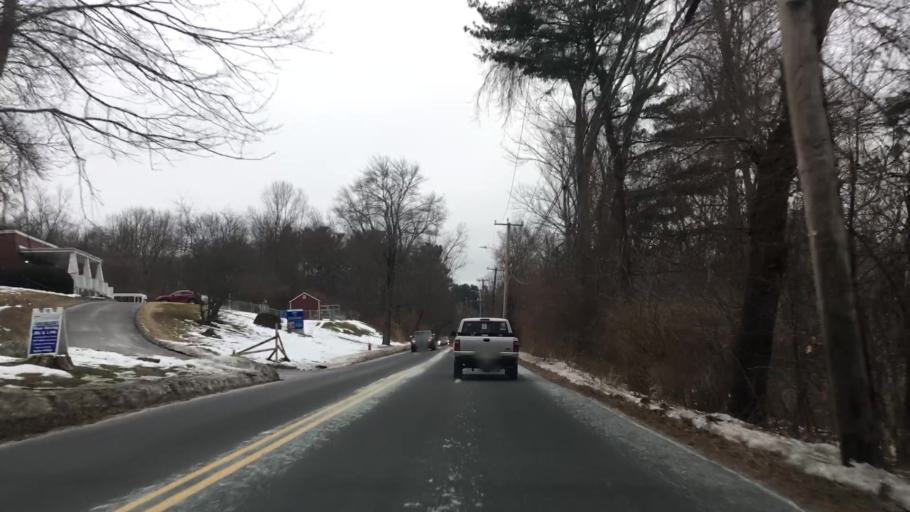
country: US
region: Massachusetts
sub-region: Hampden County
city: Westfield
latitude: 42.1006
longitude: -72.7093
